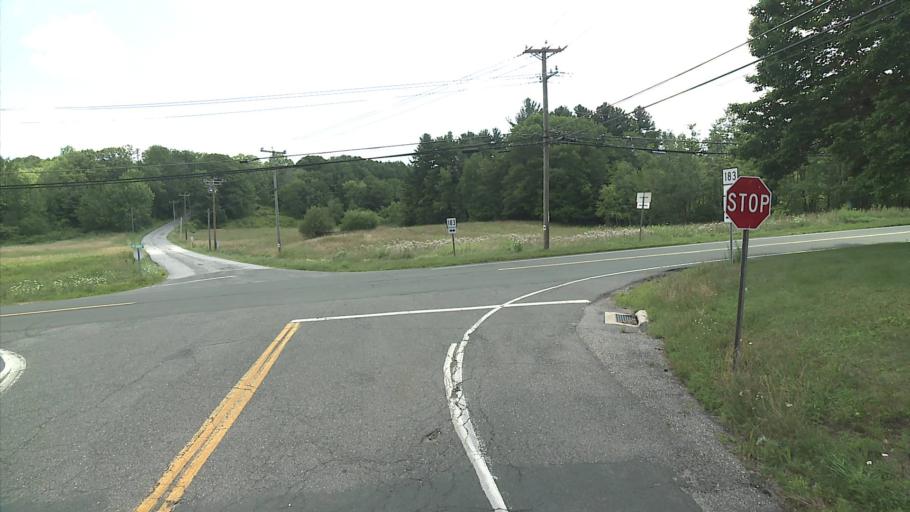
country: US
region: Connecticut
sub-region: Litchfield County
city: Winsted
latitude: 41.9793
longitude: -73.1032
